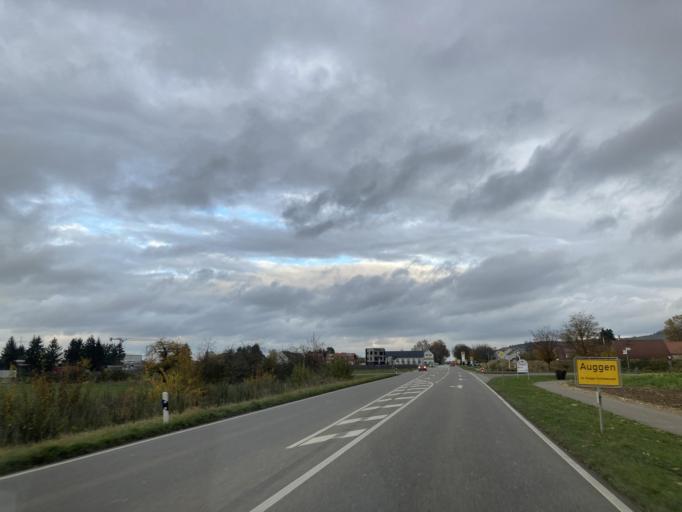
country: DE
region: Baden-Wuerttemberg
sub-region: Freiburg Region
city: Auggen
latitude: 47.7843
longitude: 7.5884
